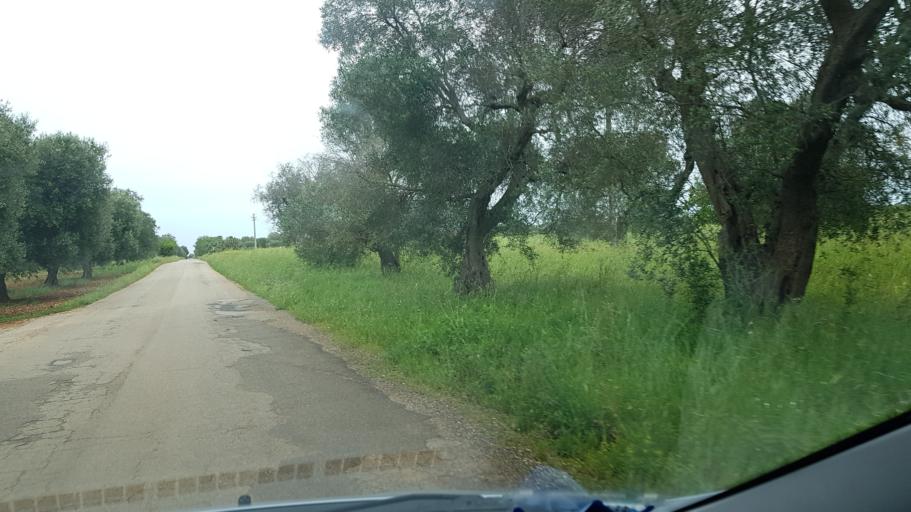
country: IT
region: Apulia
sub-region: Provincia di Brindisi
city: San Vito dei Normanni
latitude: 40.6217
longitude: 17.7622
